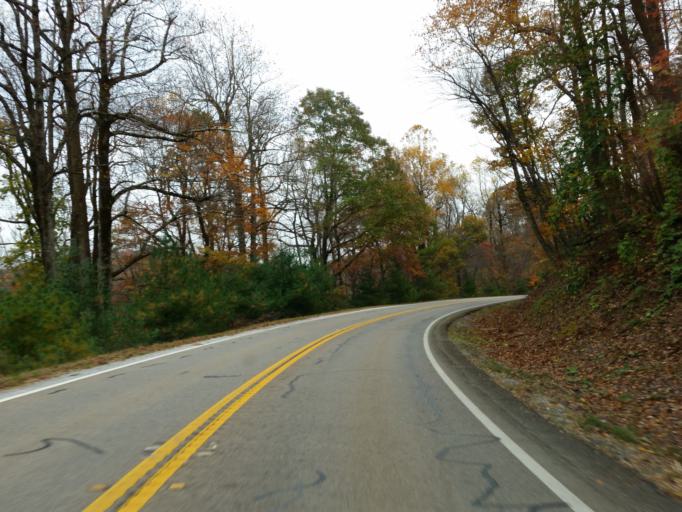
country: US
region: Georgia
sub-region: Pickens County
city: Jasper
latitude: 34.5448
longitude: -84.3638
